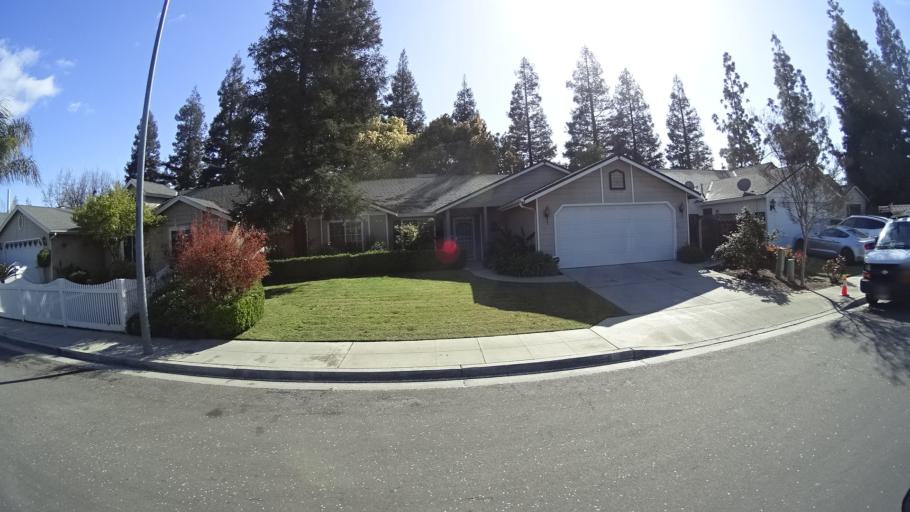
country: US
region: California
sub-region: Fresno County
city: West Park
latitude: 36.8228
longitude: -119.8728
